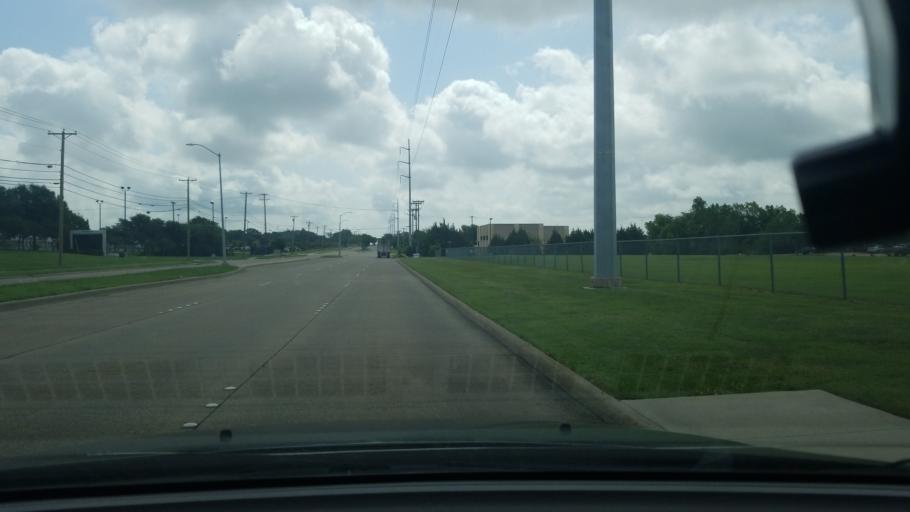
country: US
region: Texas
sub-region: Dallas County
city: Mesquite
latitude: 32.7923
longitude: -96.6778
